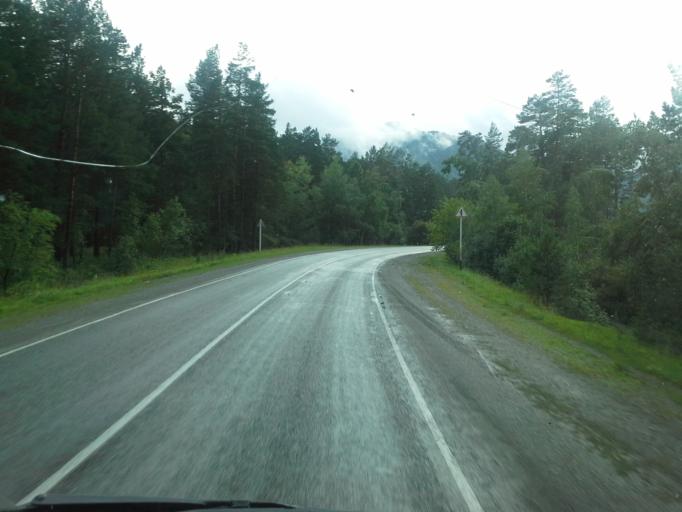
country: RU
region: Altay
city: Elekmonar
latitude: 51.5698
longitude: 85.8954
